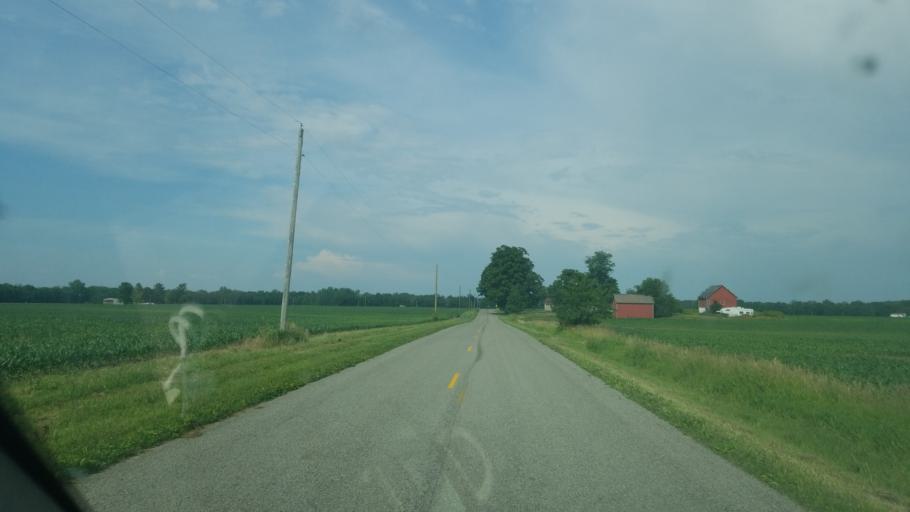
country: US
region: Ohio
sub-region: Champaign County
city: North Lewisburg
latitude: 40.1840
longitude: -83.4652
